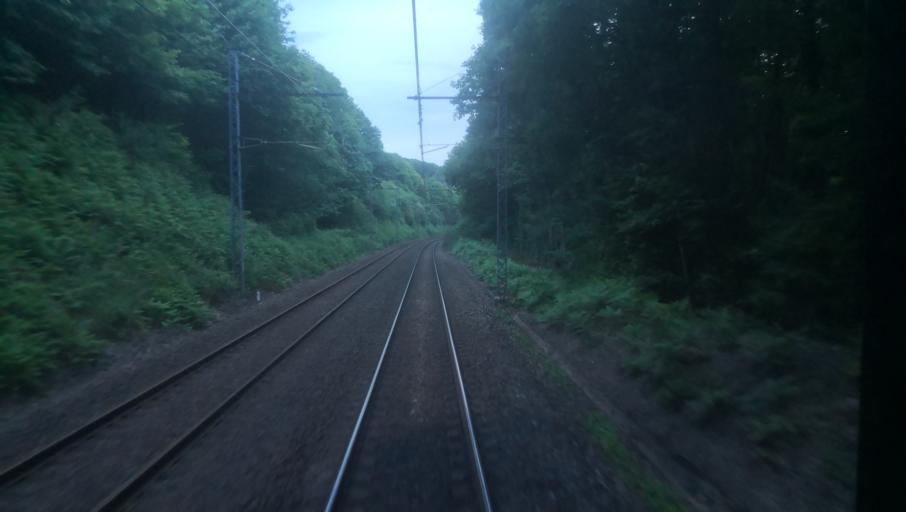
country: FR
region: Limousin
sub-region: Departement de la Haute-Vienne
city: Bessines-sur-Gartempe
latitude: 46.0559
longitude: 1.4577
